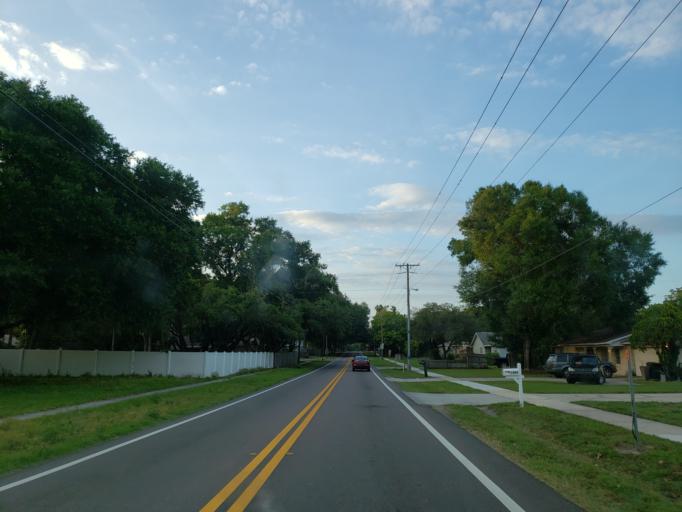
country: US
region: Florida
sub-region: Hillsborough County
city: Brandon
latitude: 27.9189
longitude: -82.2775
